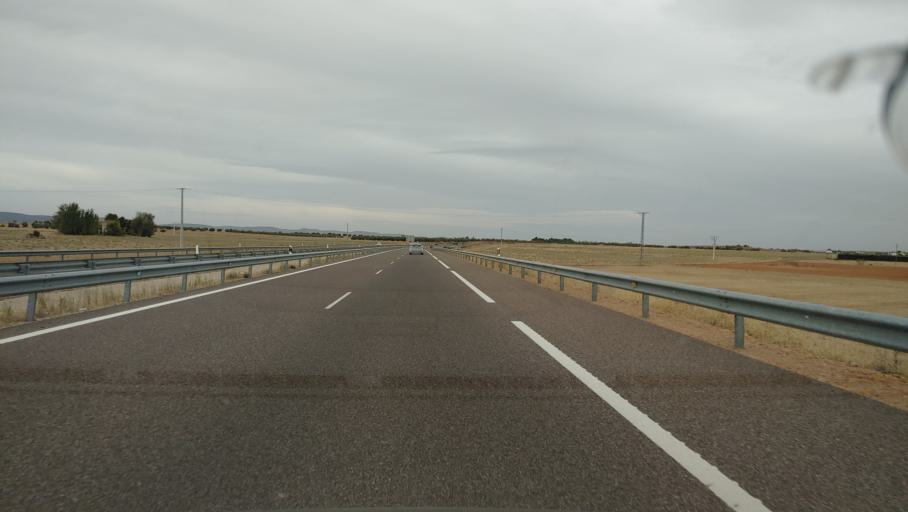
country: ES
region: Castille-La Mancha
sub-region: Provincia de Ciudad Real
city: Valenzuela de Calatrava
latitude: 38.8986
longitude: -3.8239
